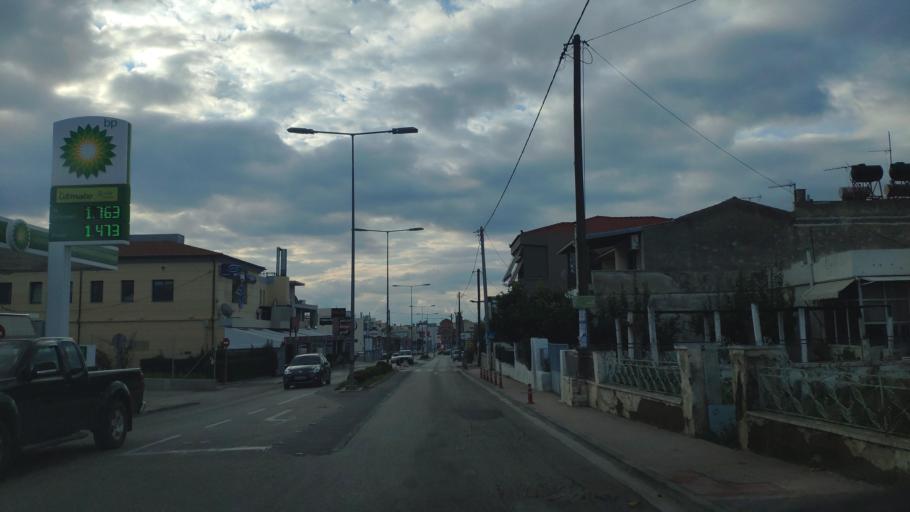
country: GR
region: Peloponnese
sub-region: Nomos Argolidos
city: Argos
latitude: 37.6456
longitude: 22.7289
